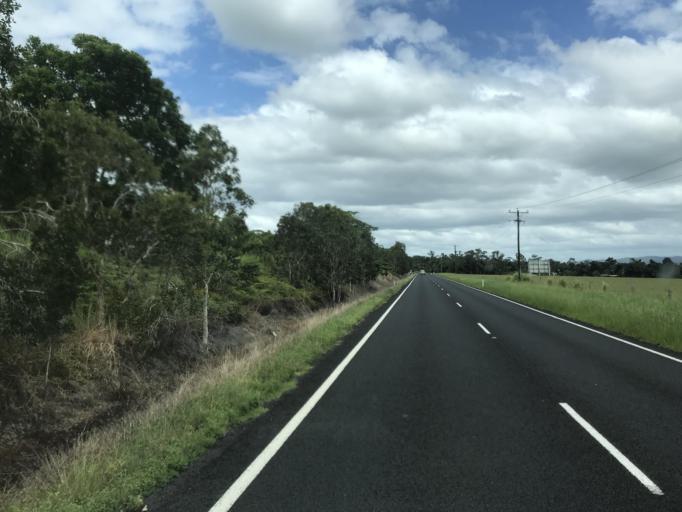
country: AU
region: Queensland
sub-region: Cassowary Coast
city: Innisfail
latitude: -17.8187
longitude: 146.0383
